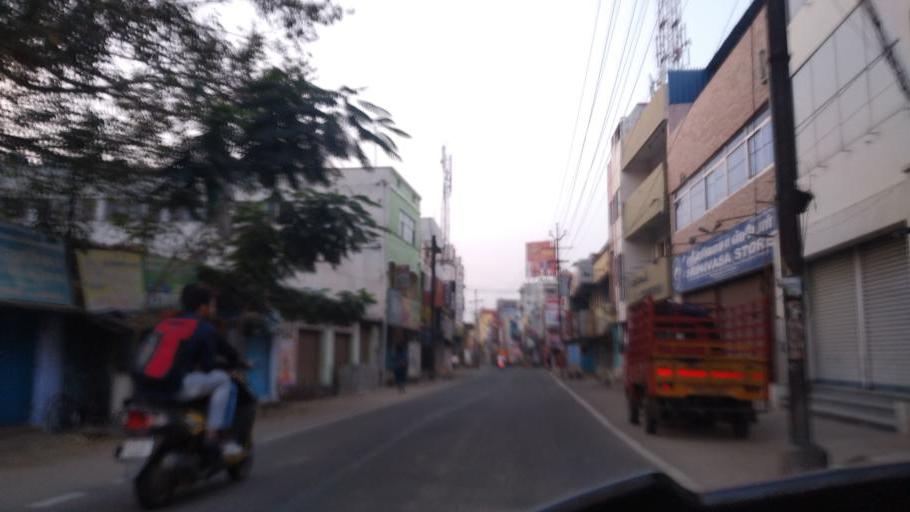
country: IN
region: Tamil Nadu
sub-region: Coimbatore
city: Coimbatore
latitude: 10.9982
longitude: 76.9600
